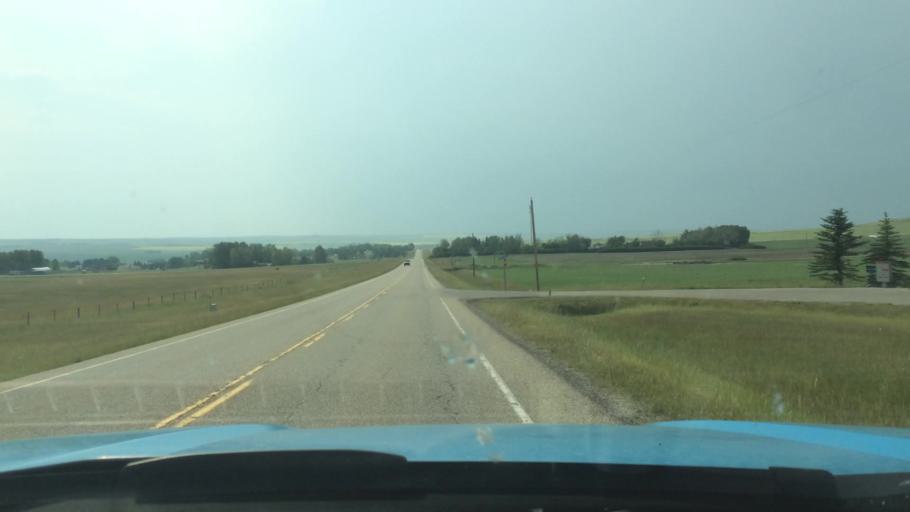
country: CA
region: Alberta
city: Airdrie
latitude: 51.2123
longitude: -114.1326
